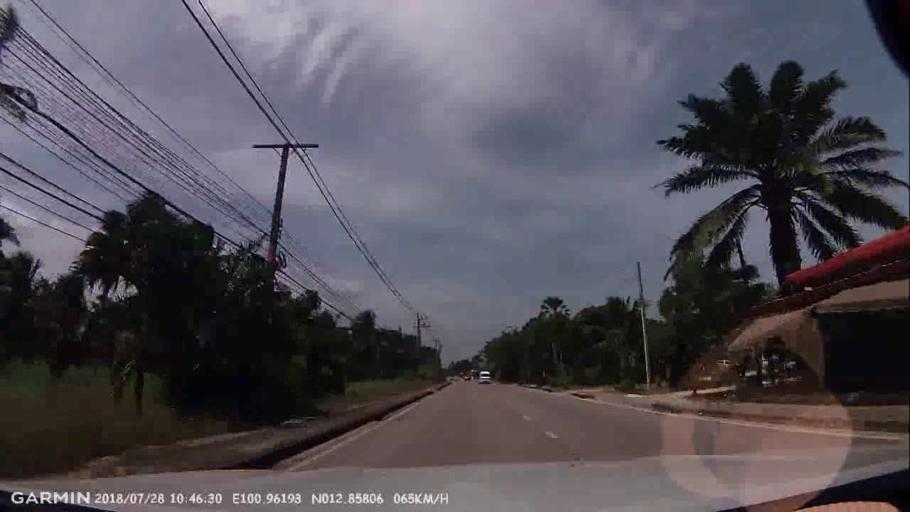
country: TH
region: Chon Buri
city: Phatthaya
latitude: 12.8578
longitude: 100.9619
